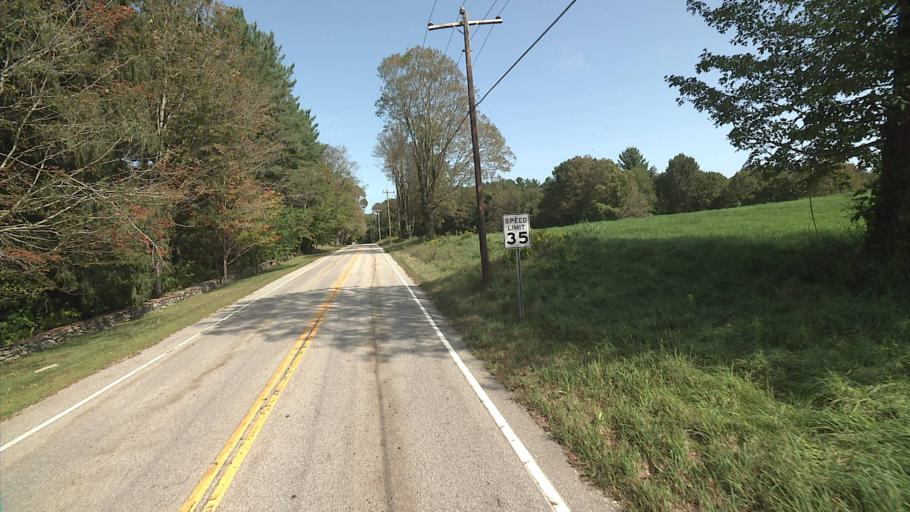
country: US
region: Connecticut
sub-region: Windham County
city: South Woodstock
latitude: 41.9140
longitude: -71.9559
